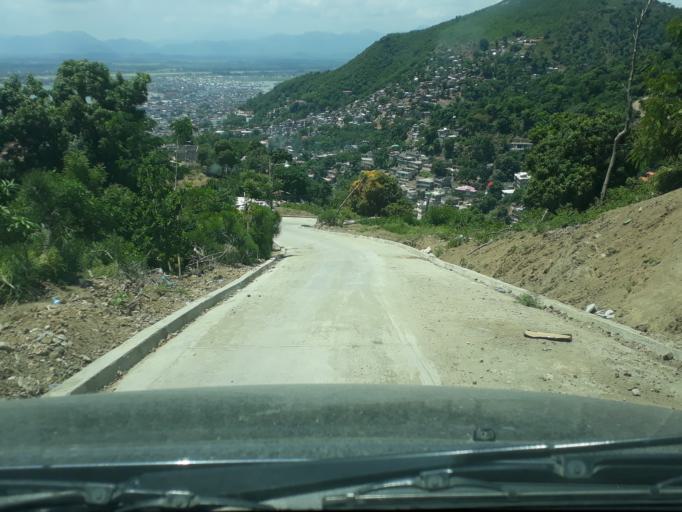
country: HT
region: Nord
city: Okap
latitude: 19.7709
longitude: -72.2070
